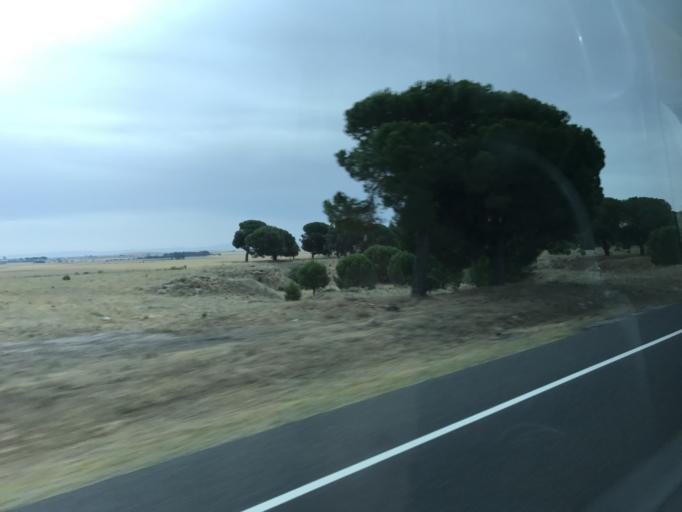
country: ES
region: Castille and Leon
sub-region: Provincia de Segovia
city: Rapariegos
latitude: 41.0692
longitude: -4.6330
